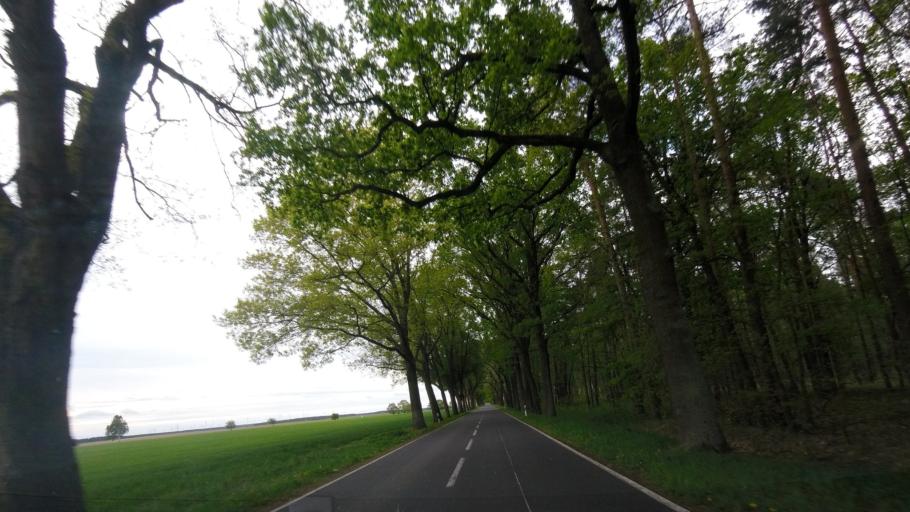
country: DE
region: Brandenburg
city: Dahme
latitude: 51.9189
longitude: 13.3952
